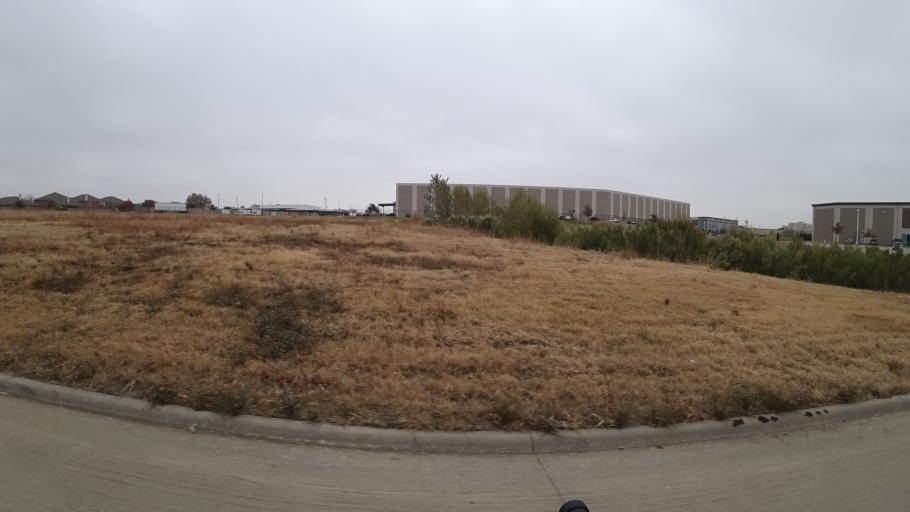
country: US
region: Texas
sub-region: Denton County
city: The Colony
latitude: 33.0627
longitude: -96.9055
